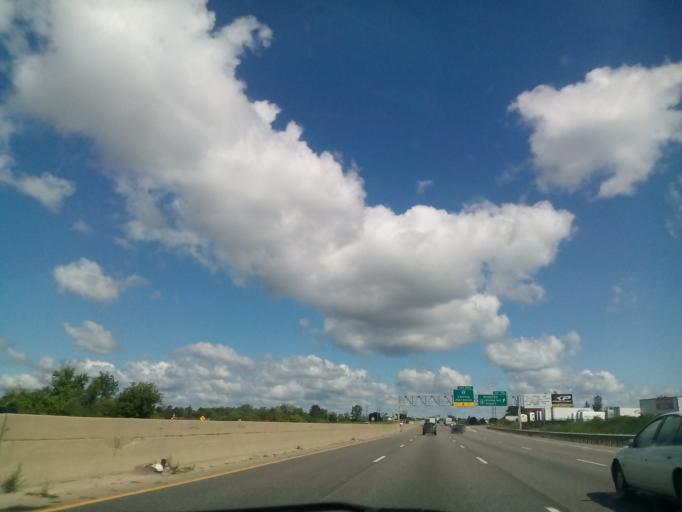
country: US
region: Michigan
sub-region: Genesee County
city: Flint
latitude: 42.9676
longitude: -83.7255
